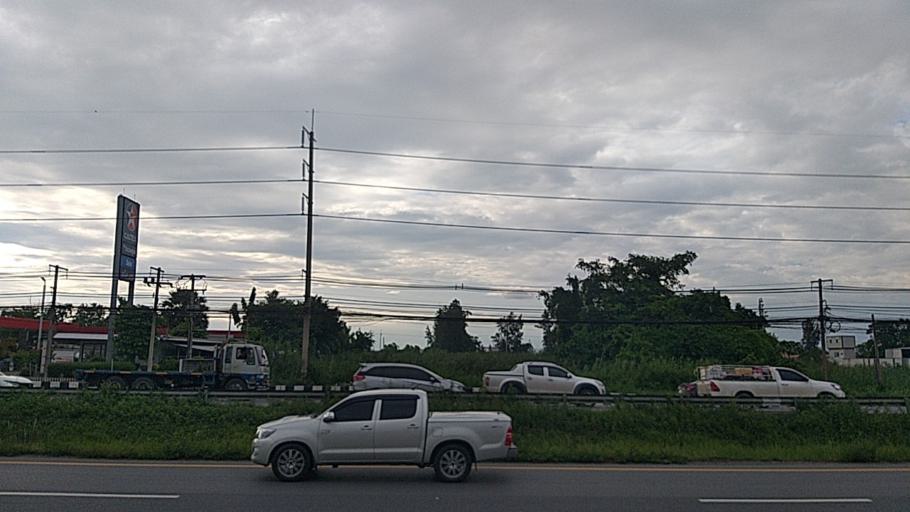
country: TH
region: Phra Nakhon Si Ayutthaya
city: Wang Noi
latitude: 14.2262
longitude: 100.7055
